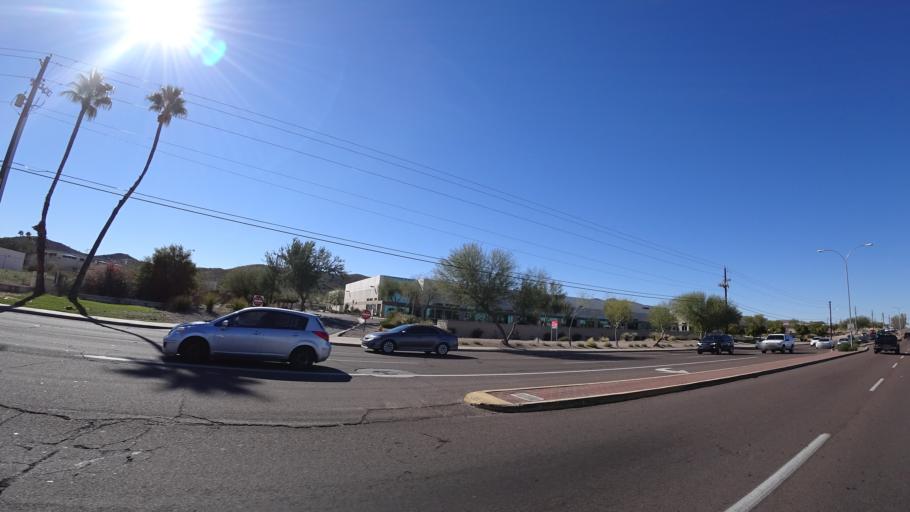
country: US
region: Arizona
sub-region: Maricopa County
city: Guadalupe
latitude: 33.3783
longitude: -111.9871
